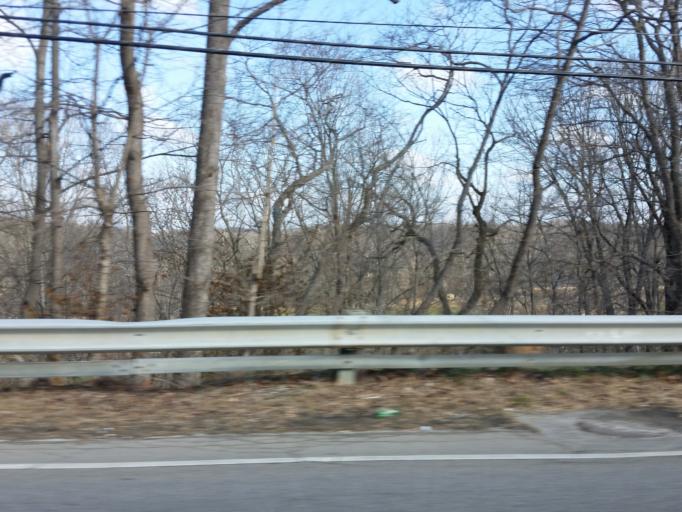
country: US
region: Indiana
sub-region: Jennings County
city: North Vernon
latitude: 38.9895
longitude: -85.6159
